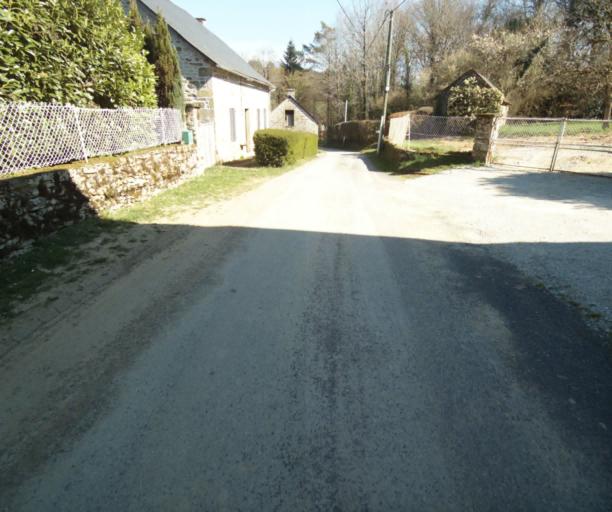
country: FR
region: Limousin
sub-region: Departement de la Correze
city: Treignac
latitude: 45.4781
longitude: 1.7680
